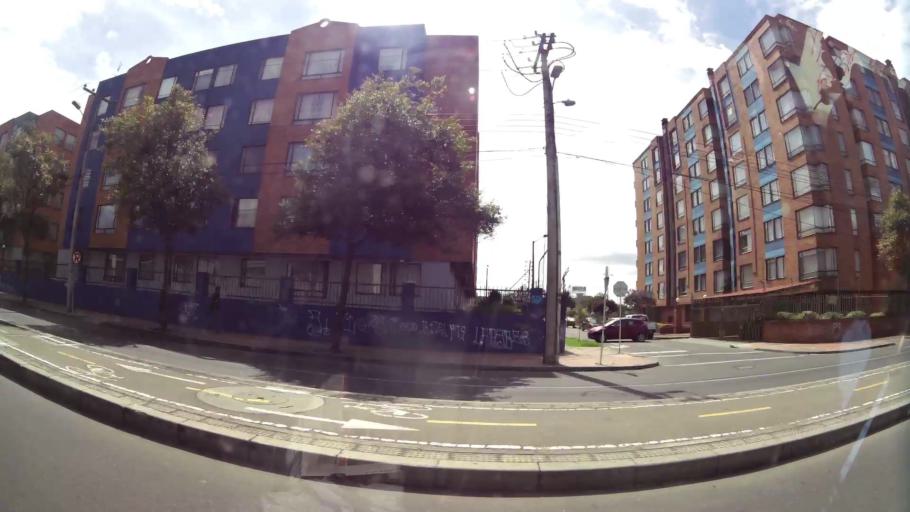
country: CO
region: Bogota D.C.
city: Bogota
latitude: 4.6292
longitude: -74.1363
